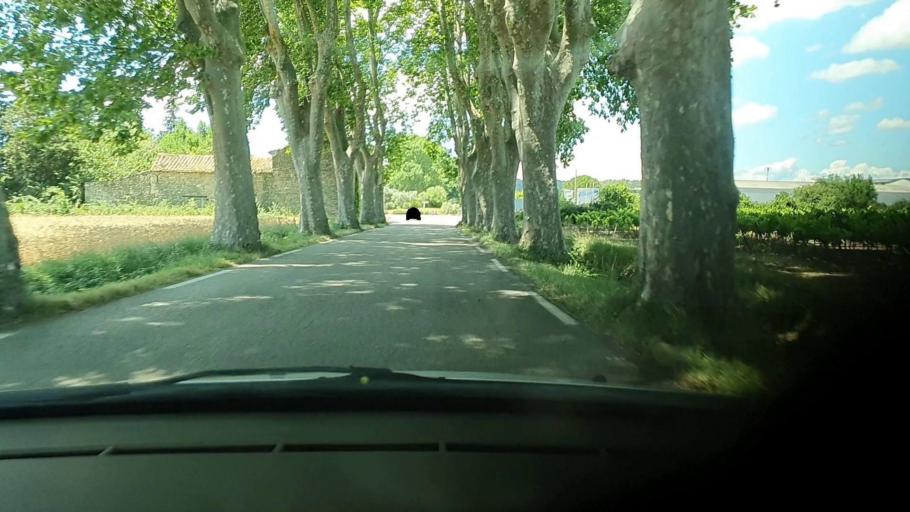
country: FR
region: Languedoc-Roussillon
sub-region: Departement du Gard
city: Montaren-et-Saint-Mediers
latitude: 44.0241
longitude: 4.3905
